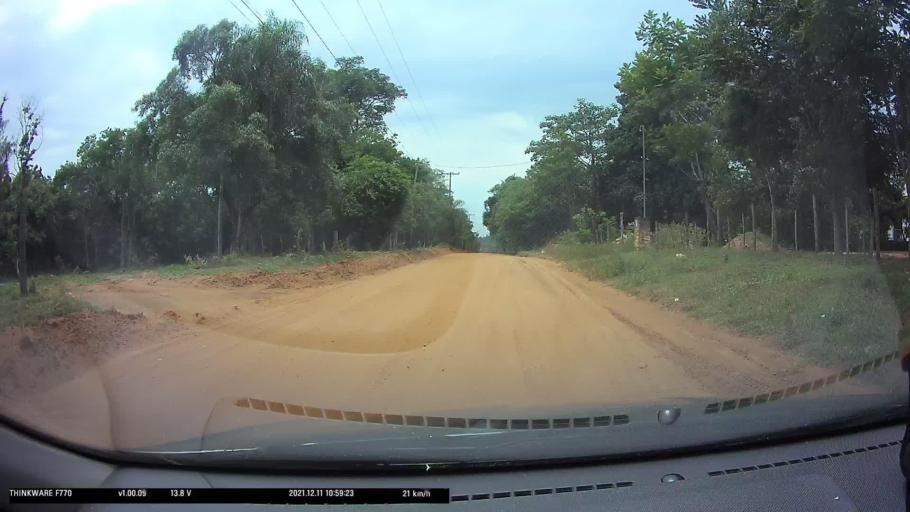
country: PY
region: Cordillera
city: San Bernardino
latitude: -25.3063
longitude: -57.2537
